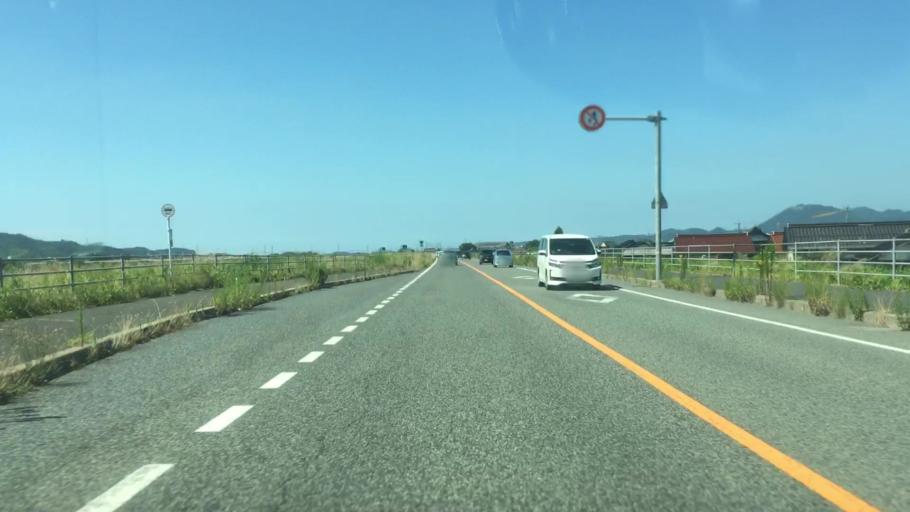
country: JP
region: Tottori
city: Tottori
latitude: 35.4564
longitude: 134.2152
